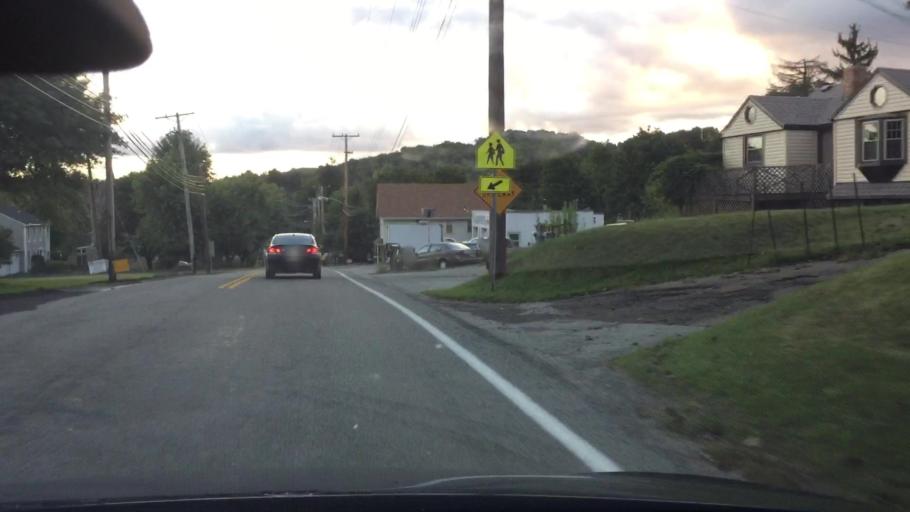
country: US
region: Pennsylvania
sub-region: Allegheny County
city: Russellton
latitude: 40.5790
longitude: -79.8858
